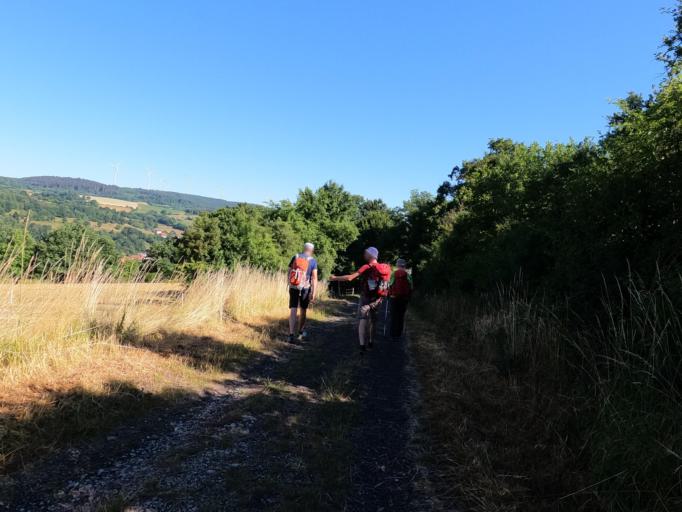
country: DE
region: Bavaria
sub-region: Regierungsbezirk Unterfranken
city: Zeitlofs
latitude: 50.3056
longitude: 9.6719
